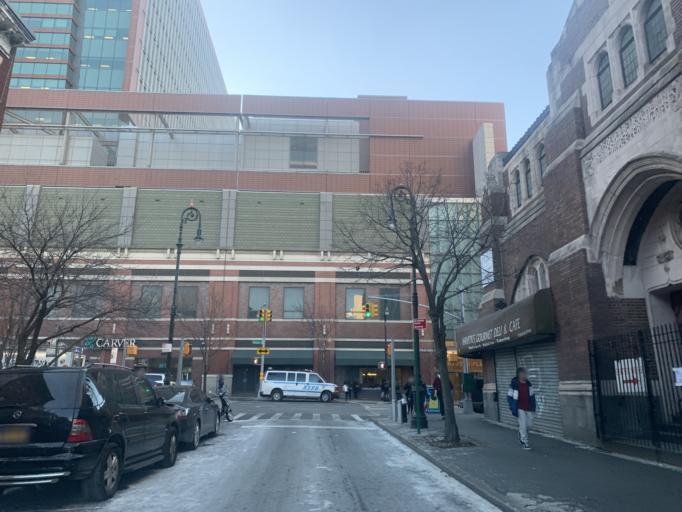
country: US
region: New York
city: New York City
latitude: 40.6856
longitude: -73.9771
